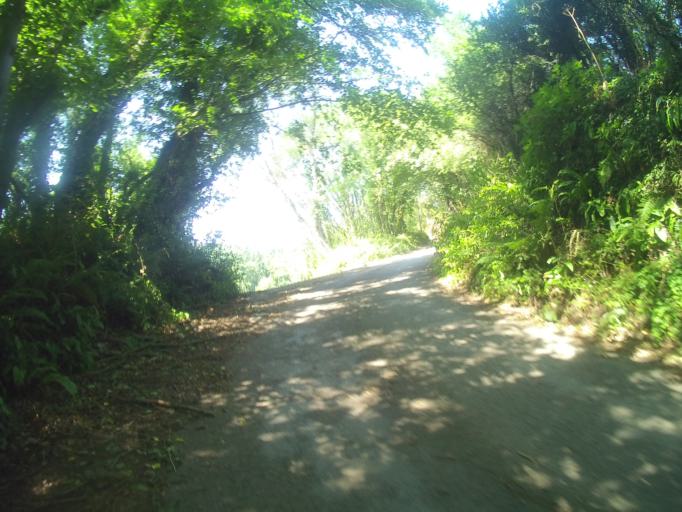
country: GB
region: England
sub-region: Devon
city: Dartmouth
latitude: 50.3591
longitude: -3.6178
